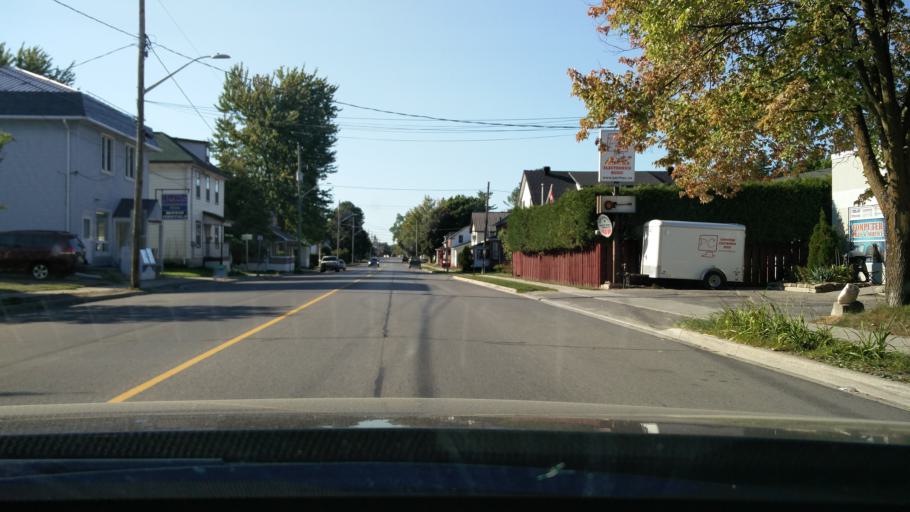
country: CA
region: Ontario
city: Perth
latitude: 44.8937
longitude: -76.2421
